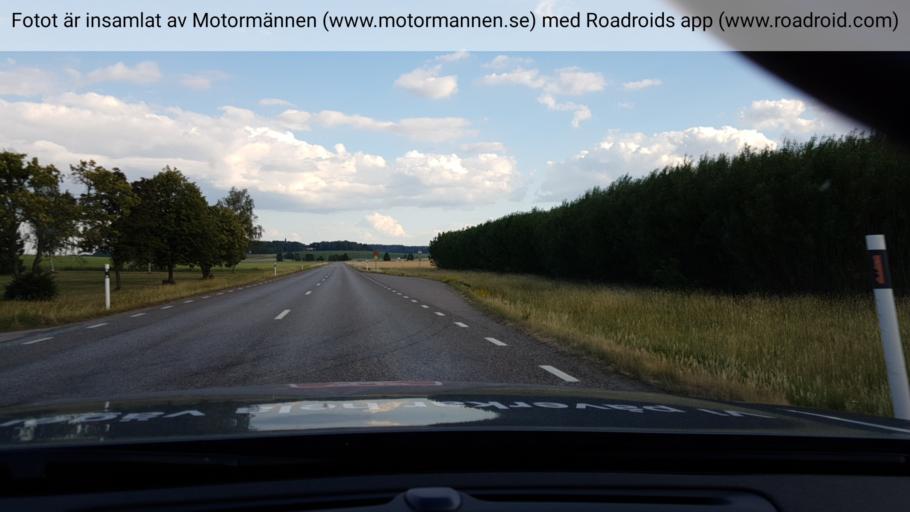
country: SE
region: Uppsala
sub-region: Heby Kommun
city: Morgongava
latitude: 59.8363
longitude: 16.9263
